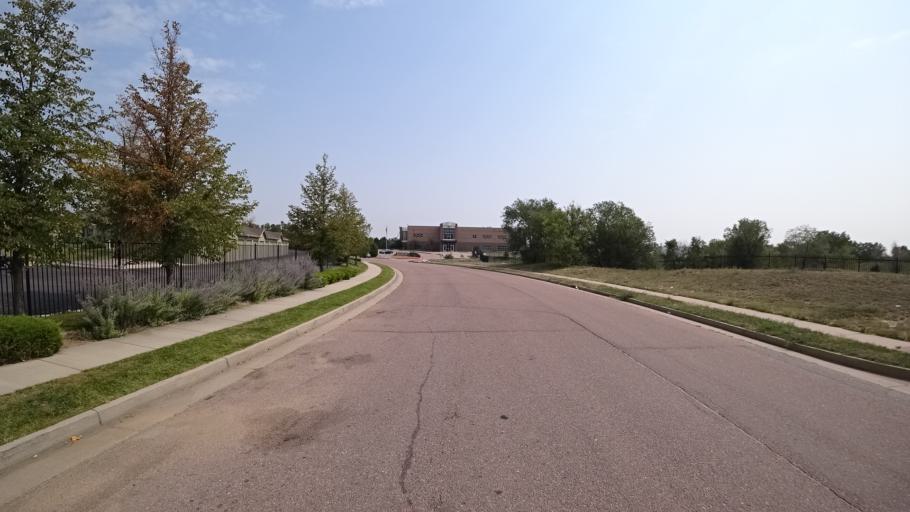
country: US
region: Colorado
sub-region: El Paso County
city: Colorado Springs
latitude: 38.8278
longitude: -104.7844
